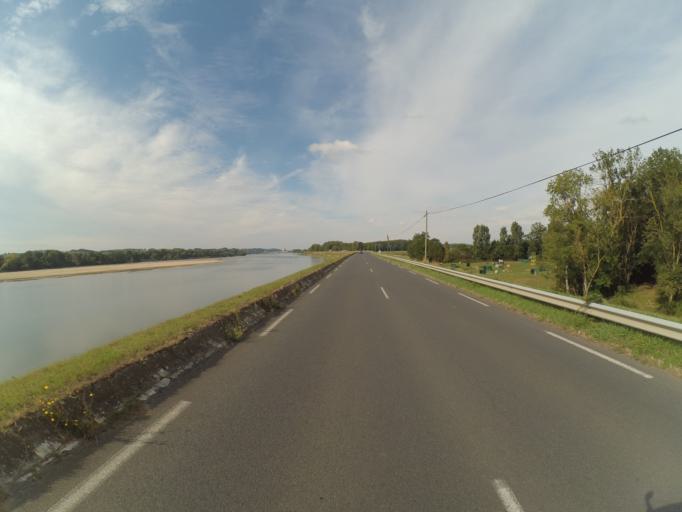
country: FR
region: Pays de la Loire
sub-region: Departement de Maine-et-Loire
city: Villebernier
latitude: 47.2470
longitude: -0.0035
